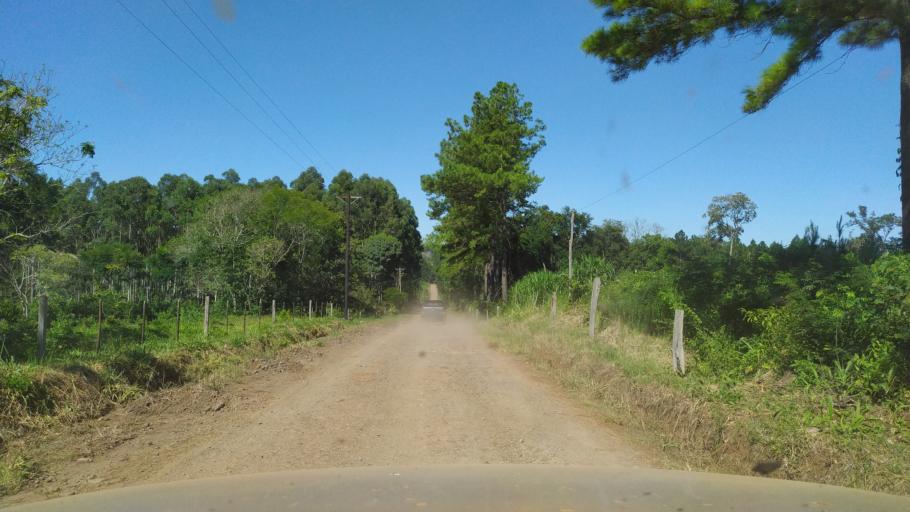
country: AR
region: Misiones
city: Caraguatay
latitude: -26.6810
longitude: -54.7077
